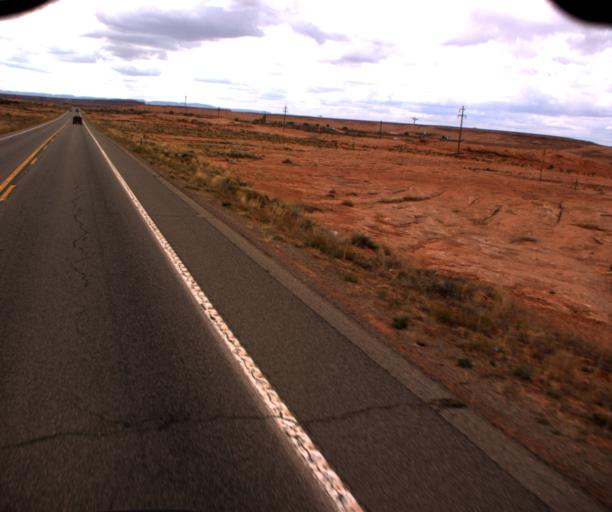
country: US
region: Arizona
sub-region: Navajo County
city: Kayenta
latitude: 36.8338
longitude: -109.8538
